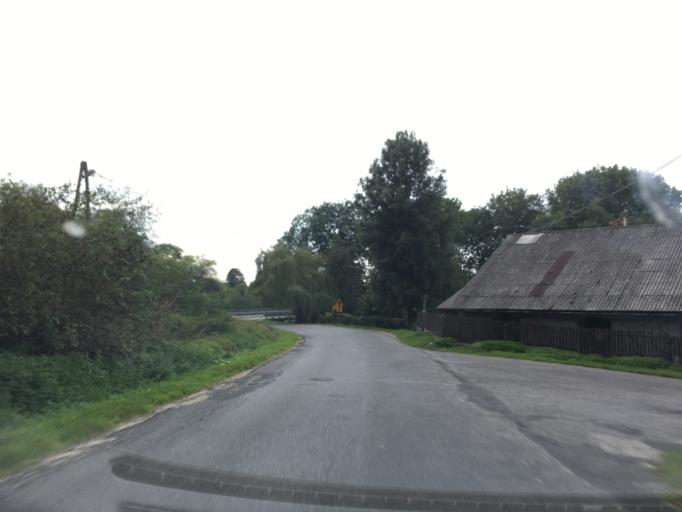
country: PL
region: Lesser Poland Voivodeship
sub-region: Powiat olkuski
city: Wolbrom
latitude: 50.4568
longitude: 19.7892
